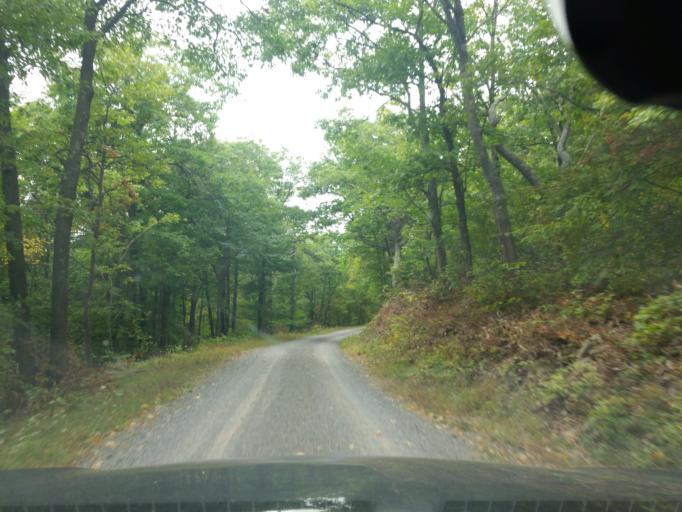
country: US
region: Pennsylvania
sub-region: Lycoming County
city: Jersey Shore
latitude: 41.0831
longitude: -77.2140
